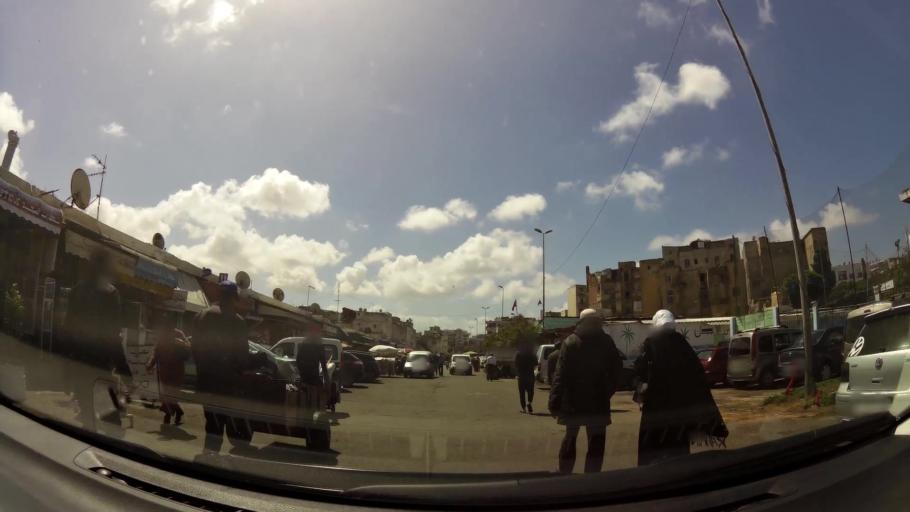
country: MA
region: Grand Casablanca
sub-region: Casablanca
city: Casablanca
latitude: 33.5991
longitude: -7.6243
